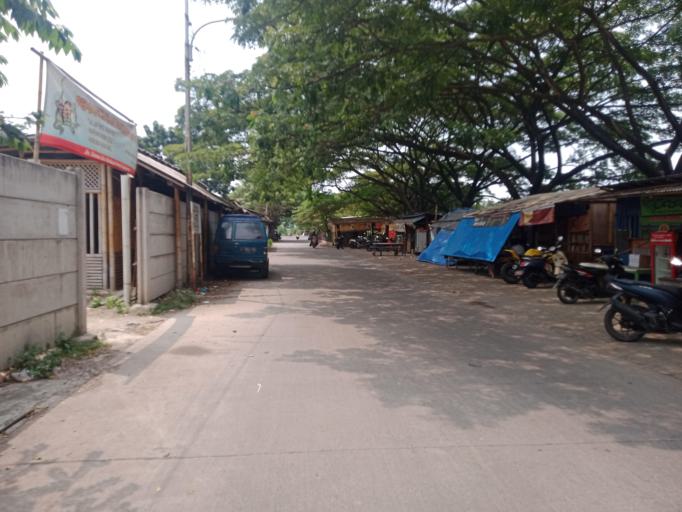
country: ID
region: Banten
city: Tangerang
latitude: -6.1628
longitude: 106.5884
